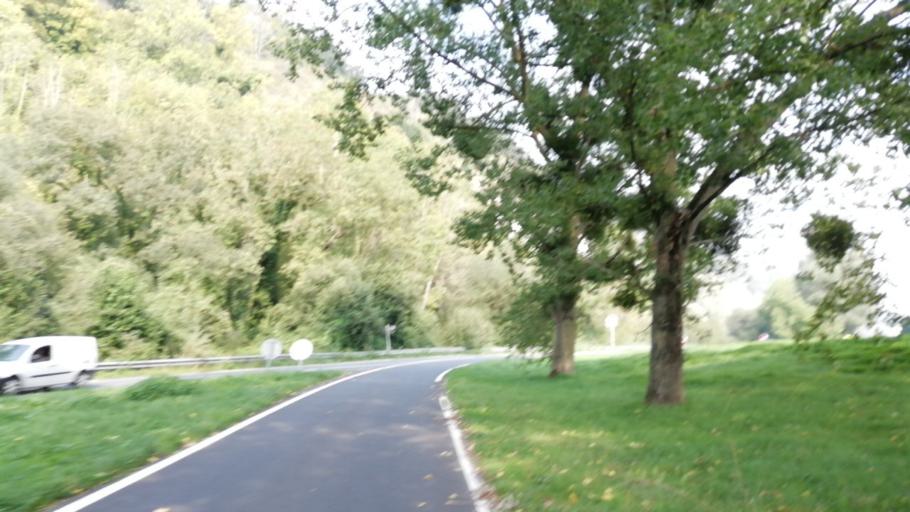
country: FR
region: Haute-Normandie
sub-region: Departement de la Seine-Maritime
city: Saint-Romain-de-Colbosc
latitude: 49.4849
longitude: 0.3579
